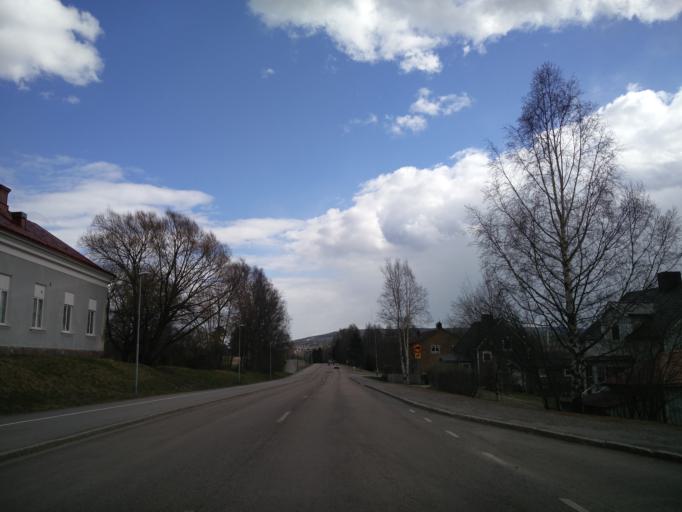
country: SE
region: Vaesternorrland
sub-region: Sundsvalls Kommun
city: Sundsvall
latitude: 62.4022
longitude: 17.2538
